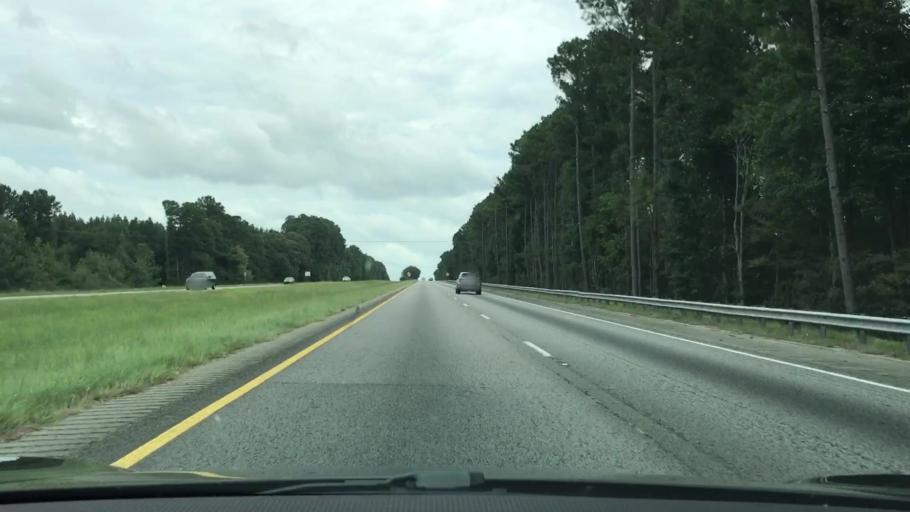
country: US
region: Georgia
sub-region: Troup County
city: La Grange
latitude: 32.9569
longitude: -85.0874
